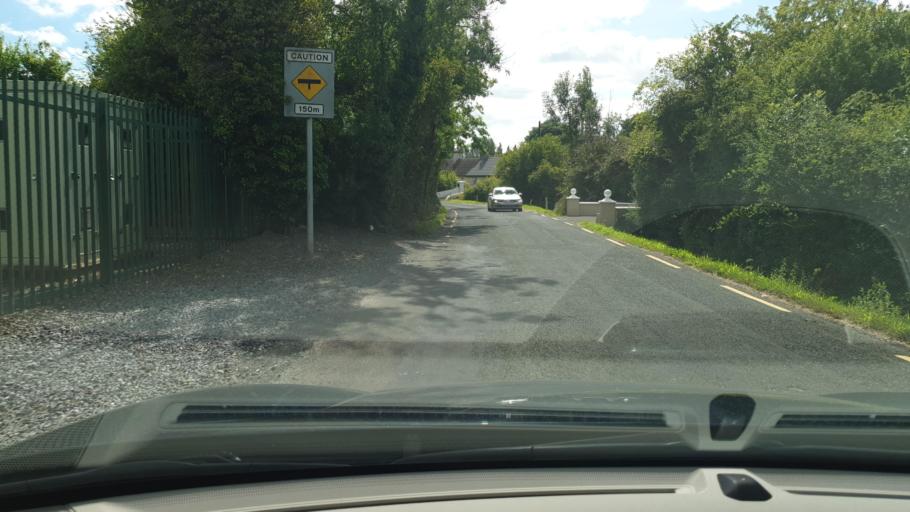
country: IE
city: Confey
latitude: 53.3767
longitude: -6.4797
